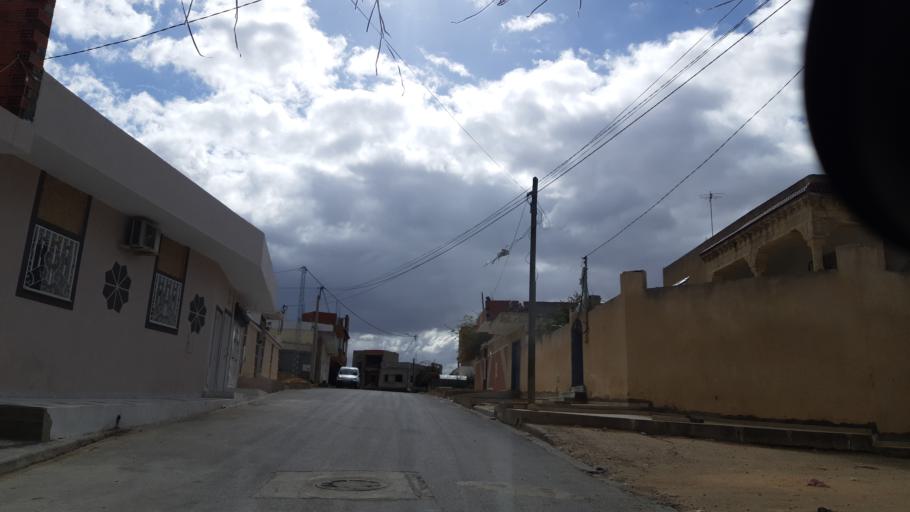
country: TN
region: Susah
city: Akouda
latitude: 35.8710
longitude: 10.5186
